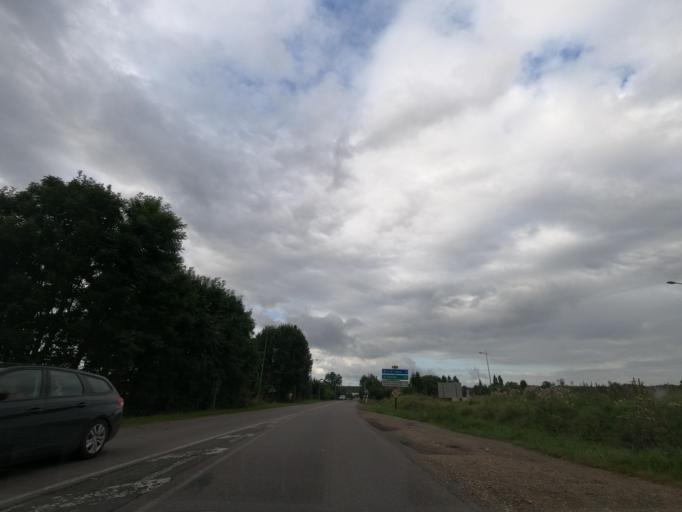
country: FR
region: Haute-Normandie
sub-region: Departement de l'Eure
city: Bourgtheroulde-Infreville
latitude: 49.3043
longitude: 0.8836
